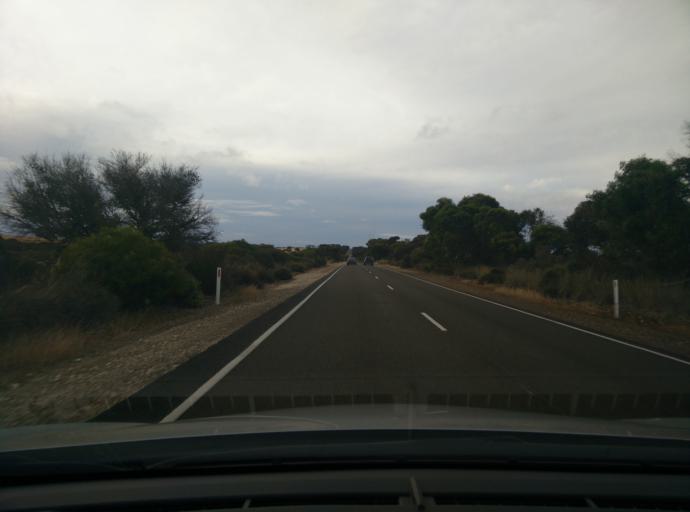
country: AU
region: South Australia
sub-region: Kangaroo Island
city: Kingscote
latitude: -35.8027
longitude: 137.6695
